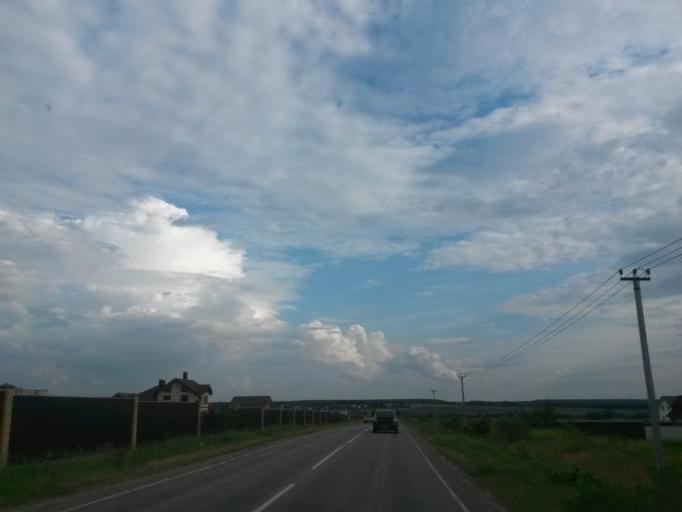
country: RU
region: Moskovskaya
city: Barybino
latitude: 55.2437
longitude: 37.7966
